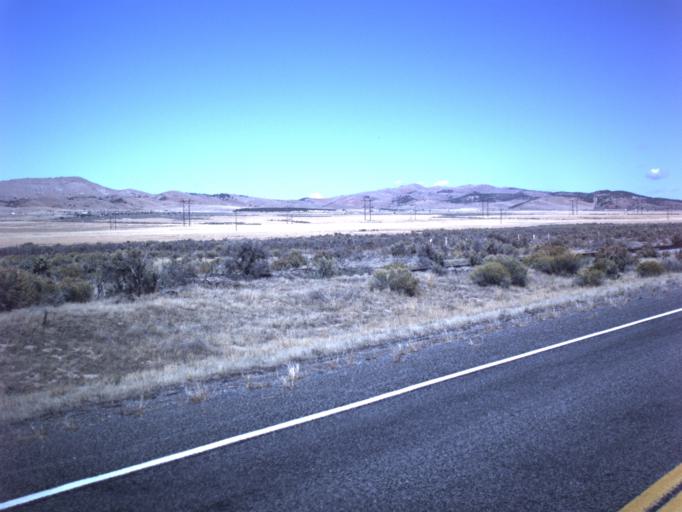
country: US
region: Utah
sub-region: Juab County
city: Nephi
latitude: 39.5427
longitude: -111.9271
